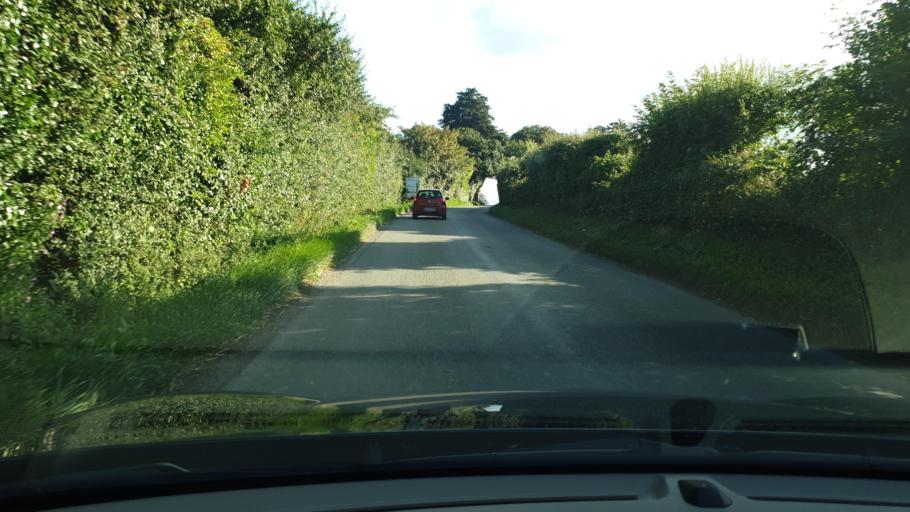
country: IE
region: Leinster
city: Lusk
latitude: 53.5405
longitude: -6.1923
